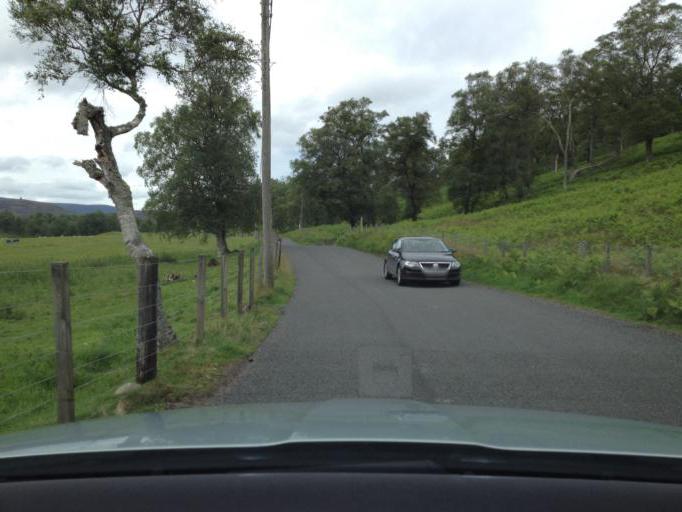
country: GB
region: Scotland
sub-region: Aberdeenshire
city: Aboyne
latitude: 56.8965
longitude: -2.7998
